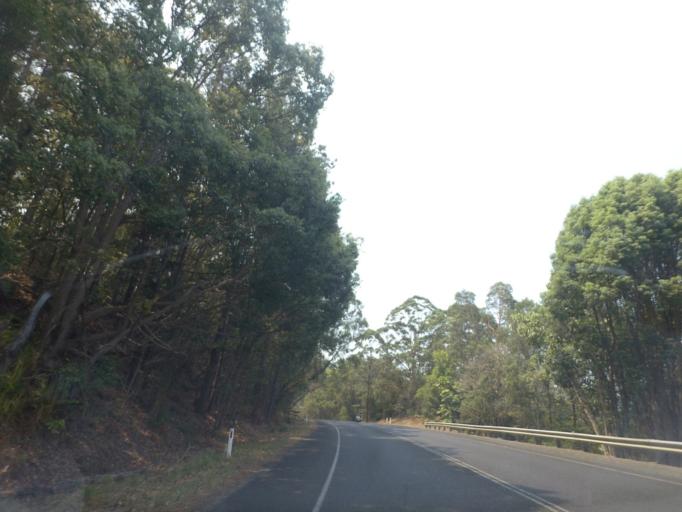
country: AU
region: New South Wales
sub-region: Byron Shire
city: Brunswick Heads
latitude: -28.5100
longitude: 153.5321
